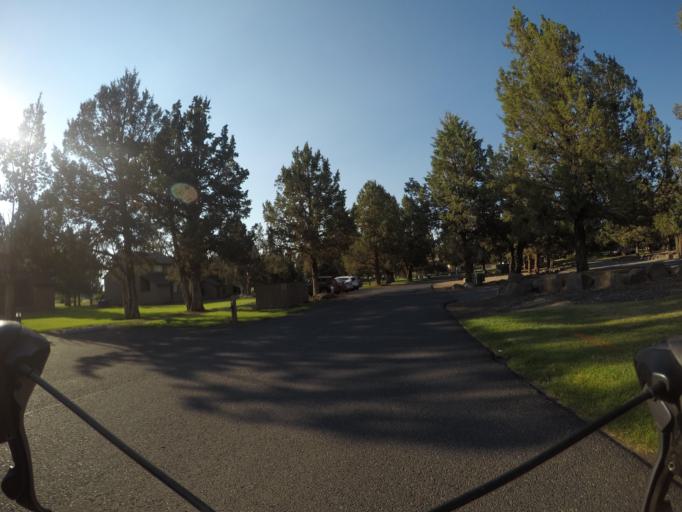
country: US
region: Oregon
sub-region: Deschutes County
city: Redmond
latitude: 44.2593
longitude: -121.2499
